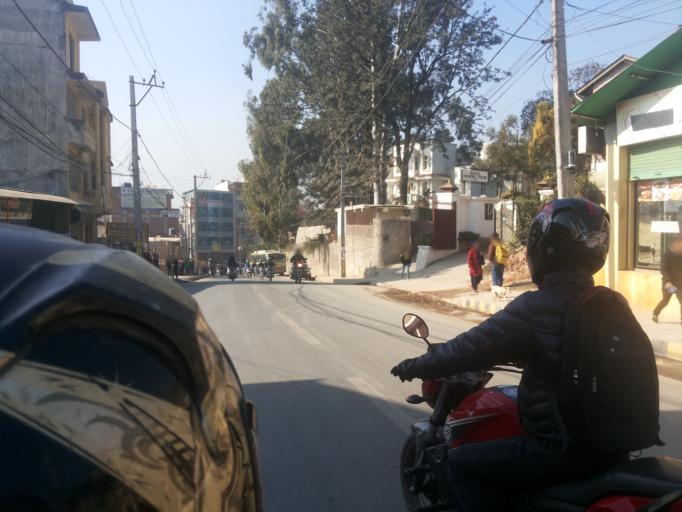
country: NP
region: Central Region
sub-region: Bagmati Zone
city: Kathmandu
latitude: 27.6852
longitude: 85.3350
